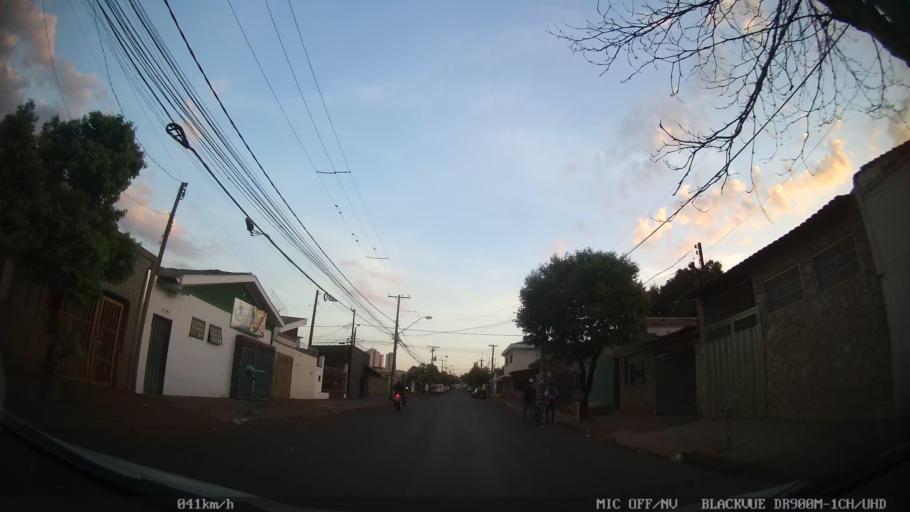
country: BR
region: Sao Paulo
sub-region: Ribeirao Preto
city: Ribeirao Preto
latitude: -21.1481
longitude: -47.8242
